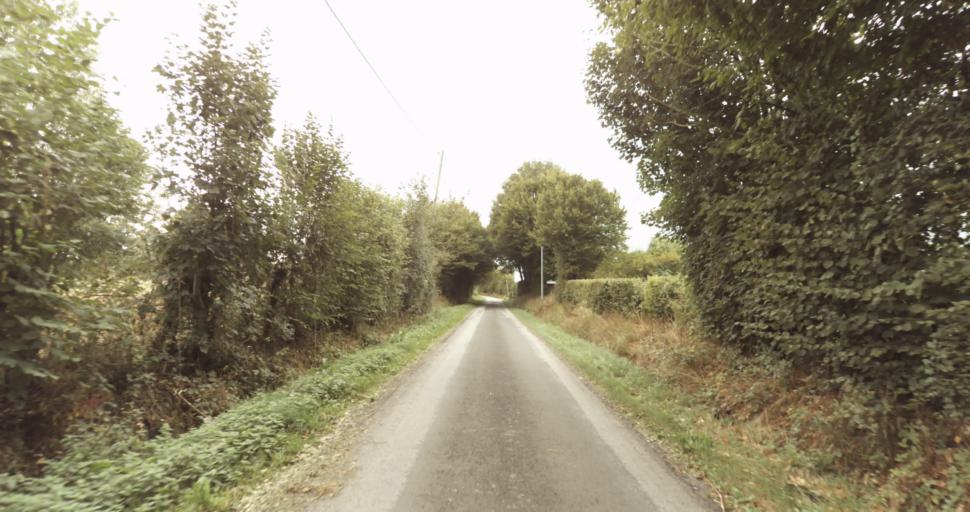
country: FR
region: Lower Normandy
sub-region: Departement de l'Orne
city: Gace
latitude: 48.7117
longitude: 0.3366
